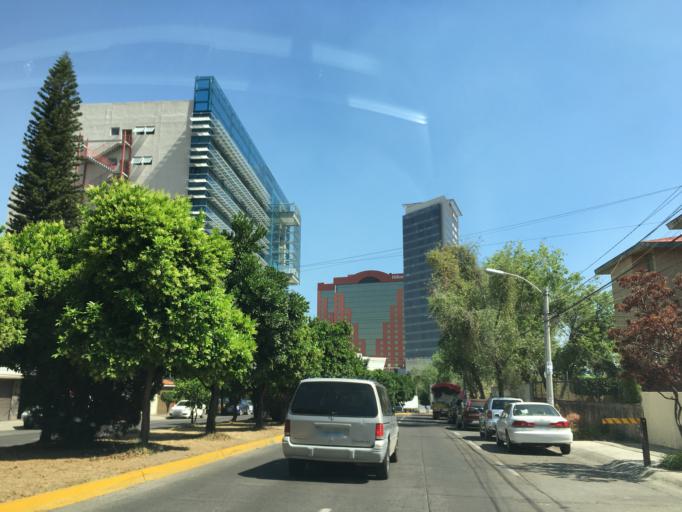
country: MX
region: Jalisco
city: Guadalajara
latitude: 20.6506
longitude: -103.3895
